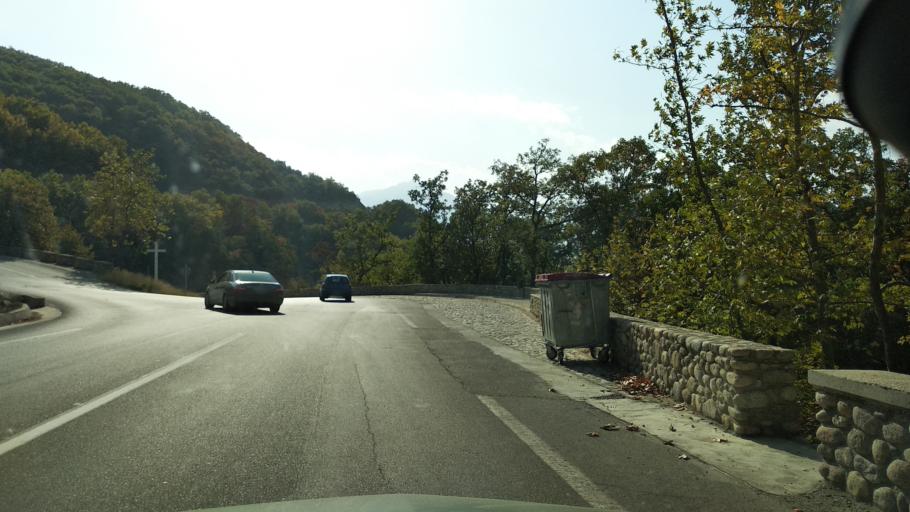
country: GR
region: Thessaly
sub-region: Trikala
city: Kastraki
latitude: 39.7257
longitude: 21.6378
